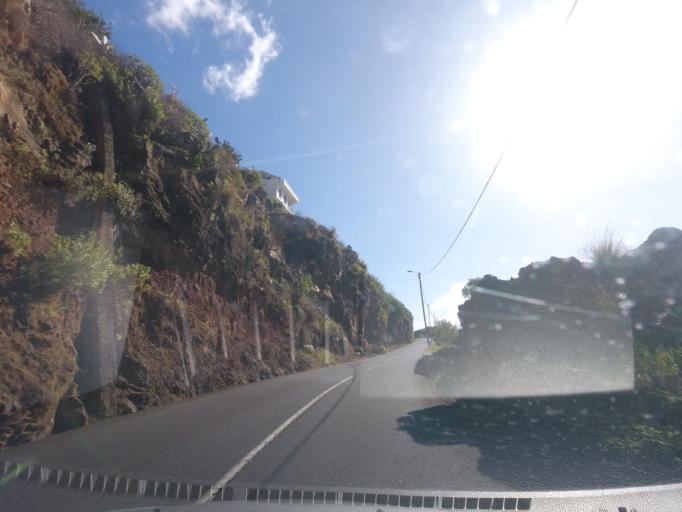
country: PT
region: Madeira
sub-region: Calheta
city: Estreito da Calheta
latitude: 32.7347
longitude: -17.1989
